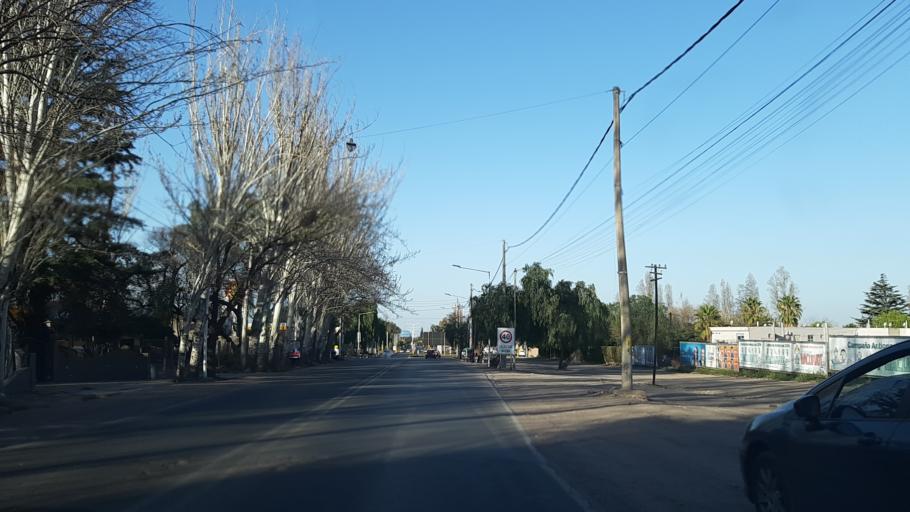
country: AR
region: Mendoza
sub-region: Departamento de Godoy Cruz
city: Godoy Cruz
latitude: -32.9624
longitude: -68.8684
